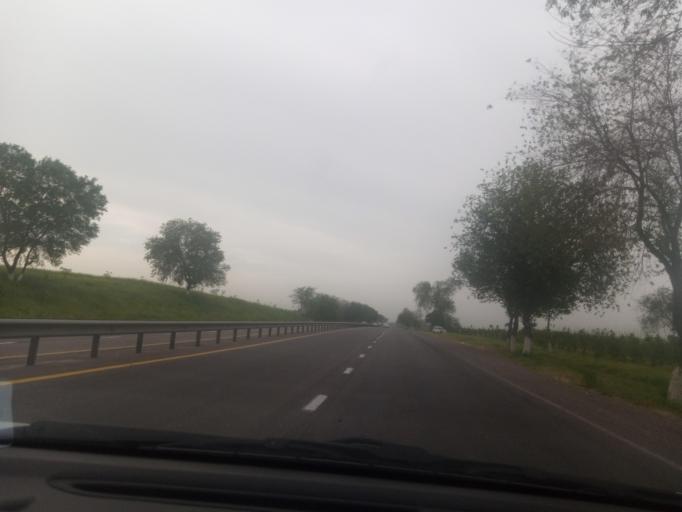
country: UZ
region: Toshkent
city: Tuytepa
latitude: 41.1078
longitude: 69.4510
